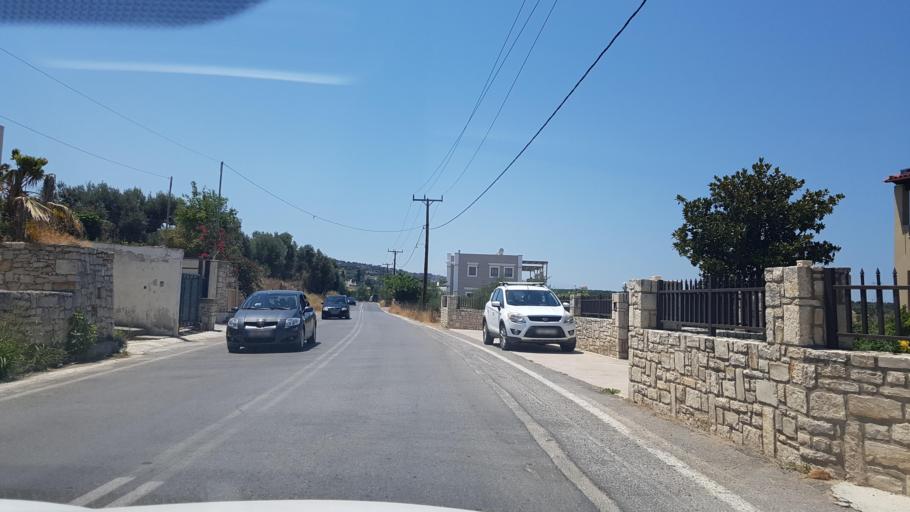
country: GR
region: Crete
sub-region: Nomos Rethymnis
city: Rethymno
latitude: 35.3585
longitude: 24.5669
